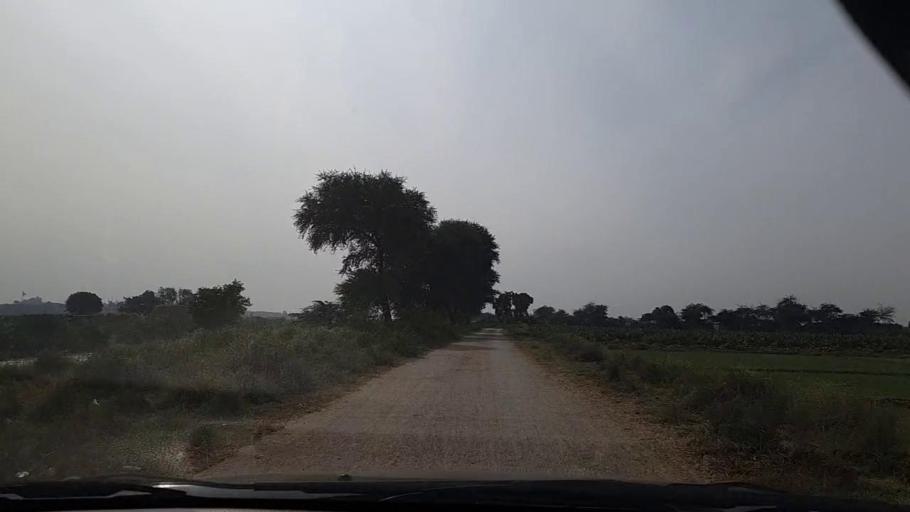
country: PK
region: Sindh
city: Thatta
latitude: 24.5755
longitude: 67.8797
